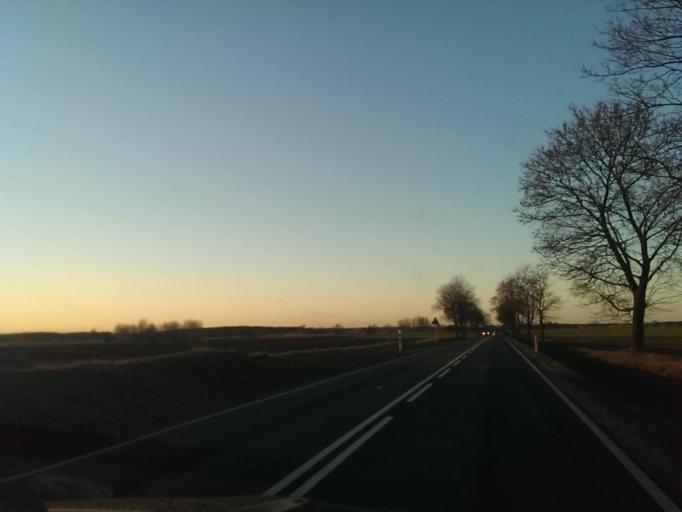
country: PL
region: Kujawsko-Pomorskie
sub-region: Powiat nakielski
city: Slesin
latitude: 53.0837
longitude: 17.6764
